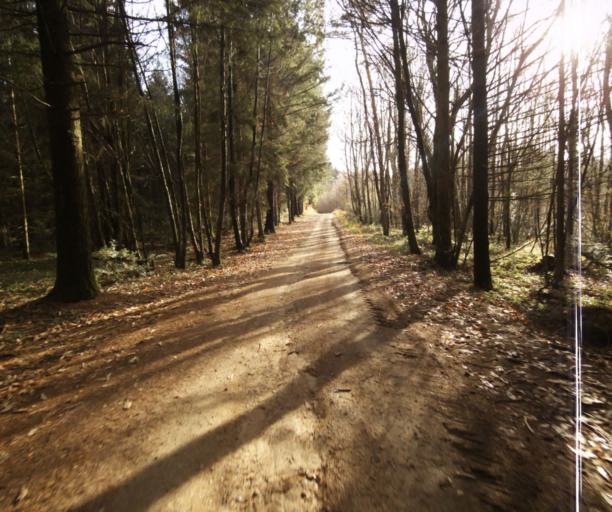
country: FR
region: Limousin
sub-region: Departement de la Correze
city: Sainte-Fortunade
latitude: 45.1944
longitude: 1.7524
